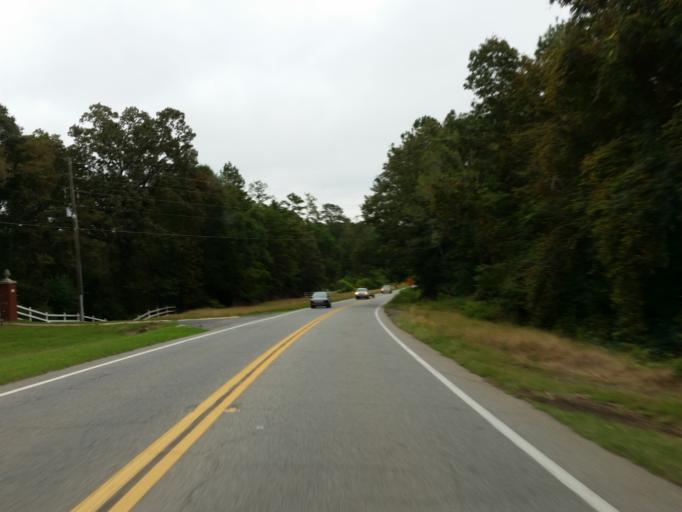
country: US
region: Georgia
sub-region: Houston County
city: Perry
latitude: 32.4863
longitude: -83.7854
